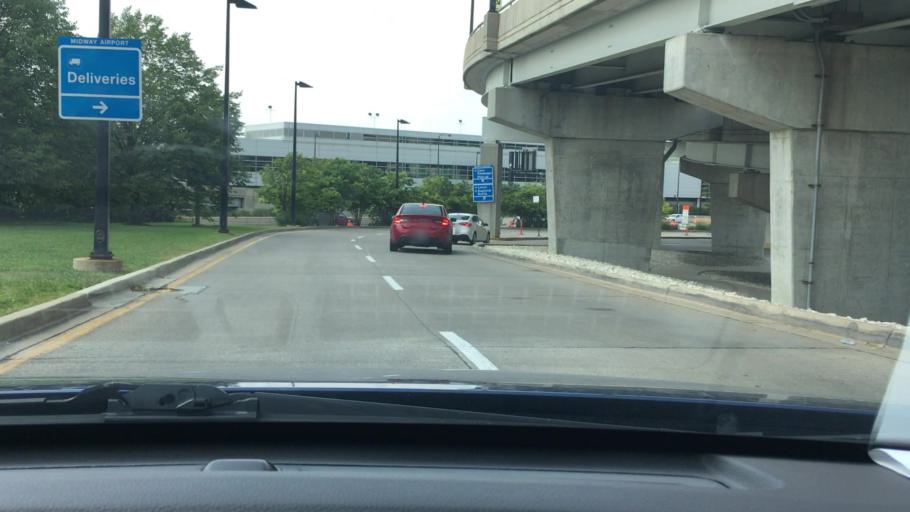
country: US
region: Illinois
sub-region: Cook County
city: Hometown
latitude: 41.7862
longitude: -87.7403
